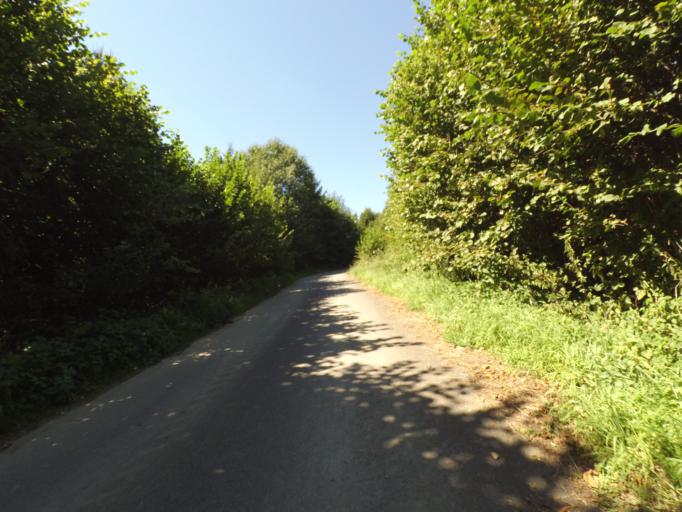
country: DE
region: Rheinland-Pfalz
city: Wagenhausen
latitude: 50.1570
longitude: 6.9976
